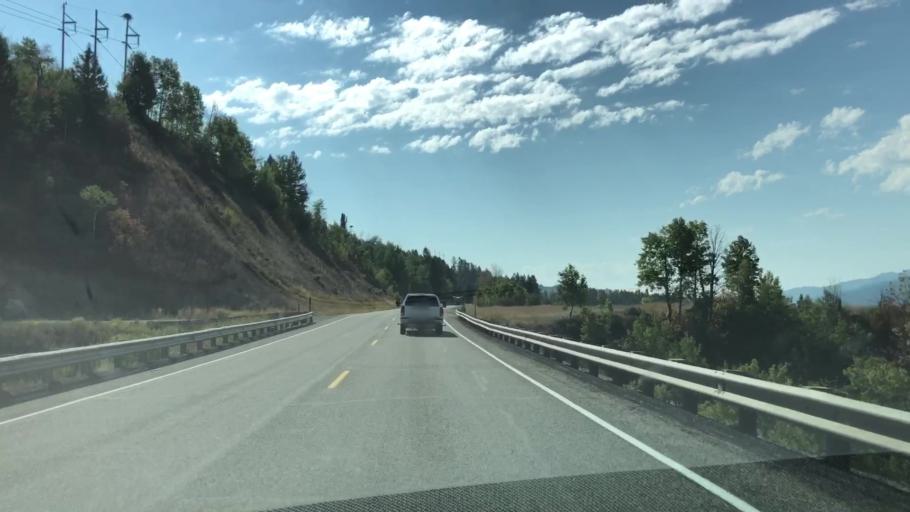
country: US
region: Idaho
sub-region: Teton County
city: Victor
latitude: 43.2937
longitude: -111.1256
